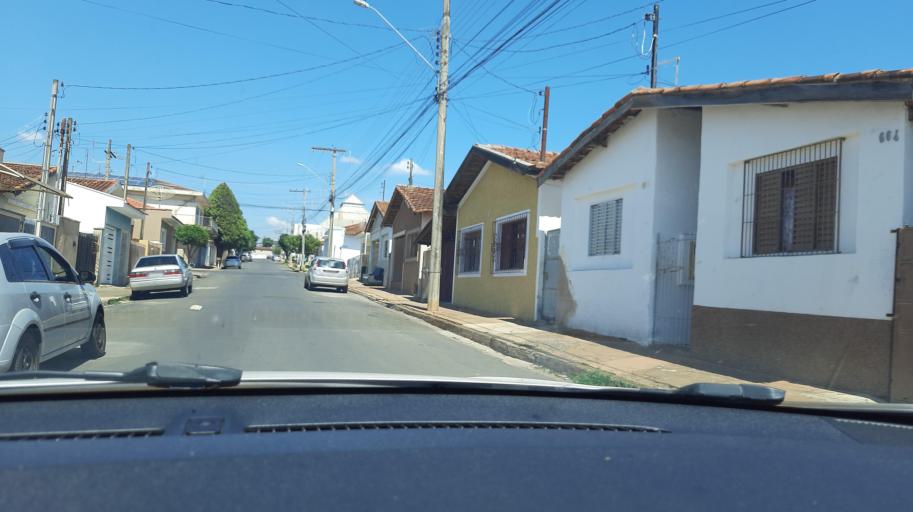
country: BR
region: Sao Paulo
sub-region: Vargem Grande Do Sul
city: Vargem Grande do Sul
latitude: -21.8423
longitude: -46.9000
